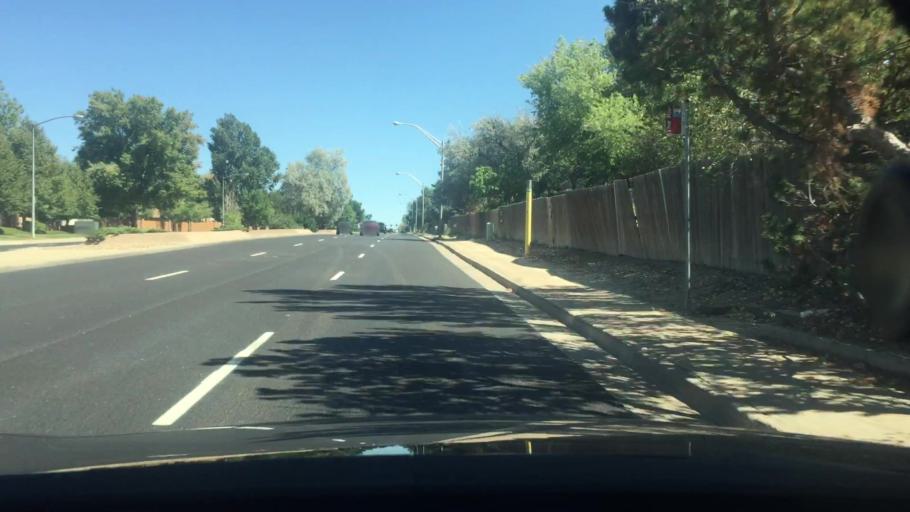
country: US
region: Colorado
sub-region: Arapahoe County
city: Dove Valley
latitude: 39.6385
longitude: -104.8160
